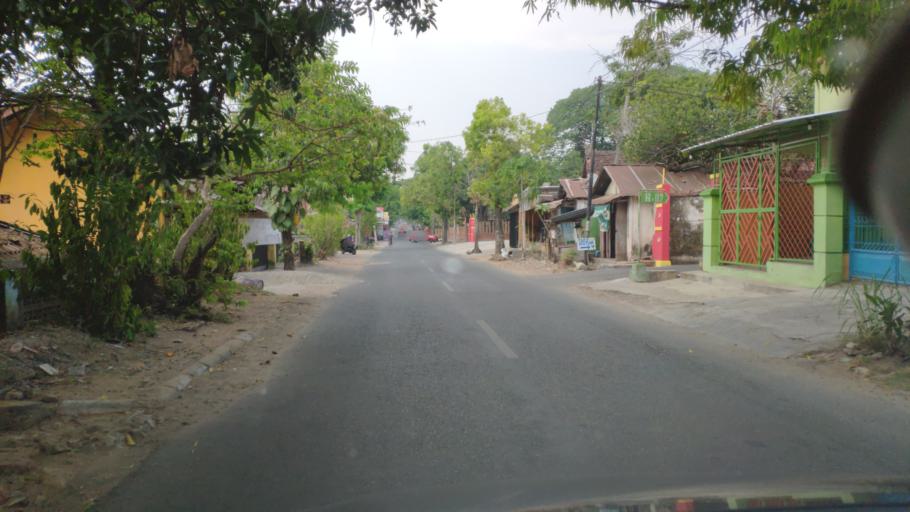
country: ID
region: Central Java
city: Kunden
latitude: -6.9631
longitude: 111.4132
